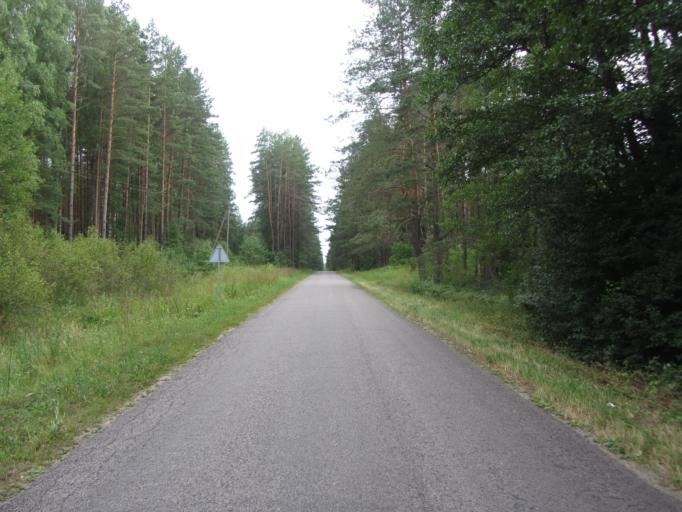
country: LT
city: Veisiejai
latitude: 54.0173
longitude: 23.7246
